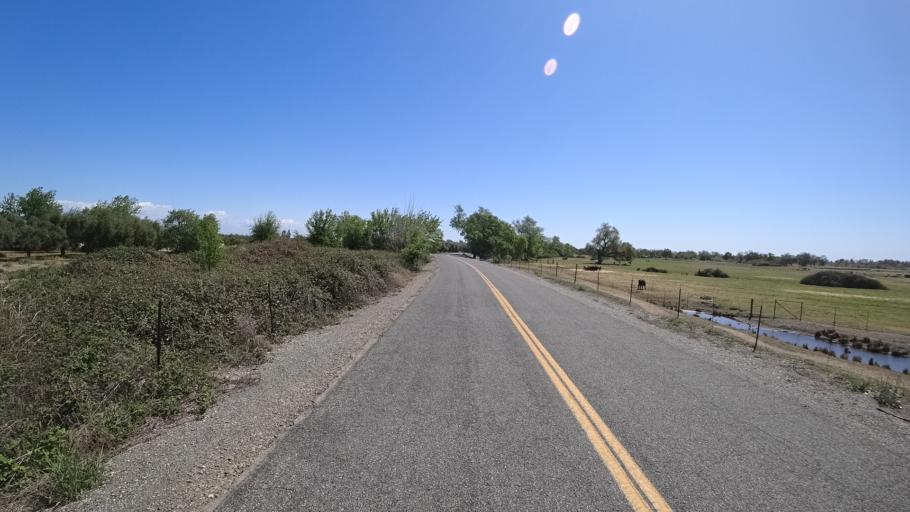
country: US
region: California
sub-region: Glenn County
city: Orland
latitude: 39.7879
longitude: -122.2215
